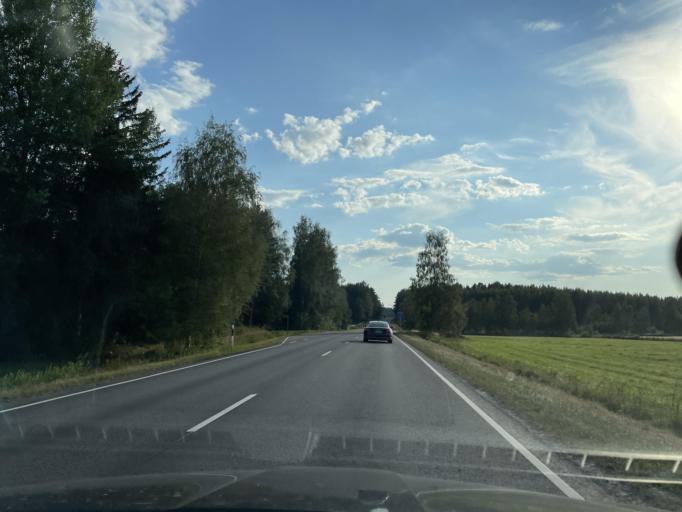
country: FI
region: Haeme
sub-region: Haemeenlinna
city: Tuulos
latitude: 61.1100
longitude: 24.8763
